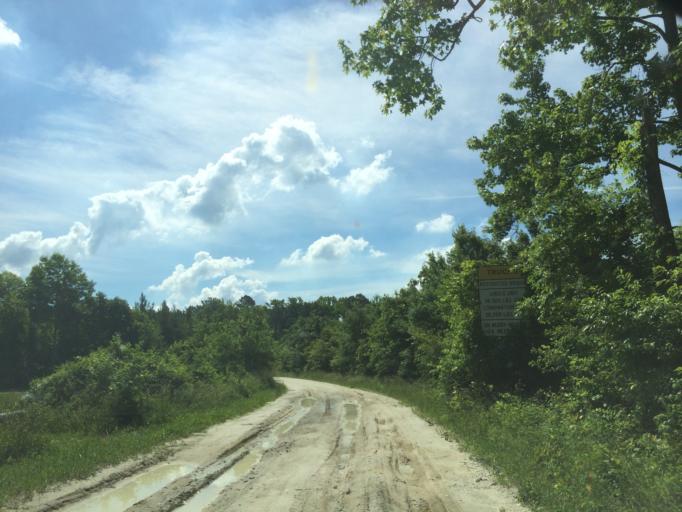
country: US
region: Maryland
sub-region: Somerset County
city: Princess Anne
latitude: 38.2895
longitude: -75.8775
